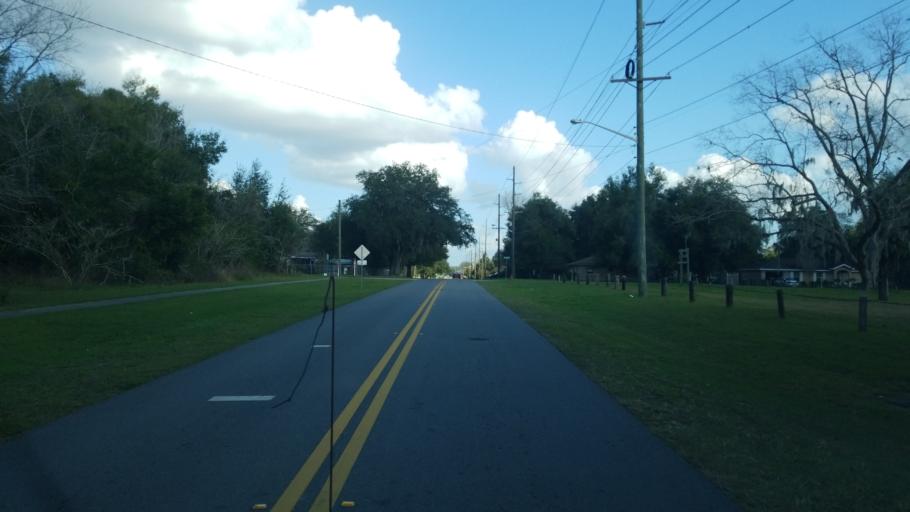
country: US
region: Florida
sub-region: Marion County
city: Ocala
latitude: 29.1826
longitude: -82.1655
